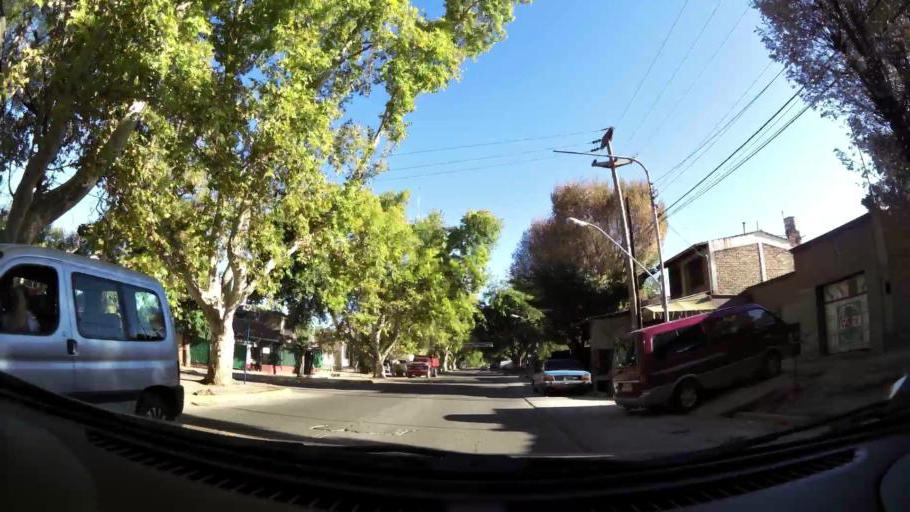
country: AR
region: Mendoza
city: Las Heras
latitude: -32.8554
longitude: -68.8270
